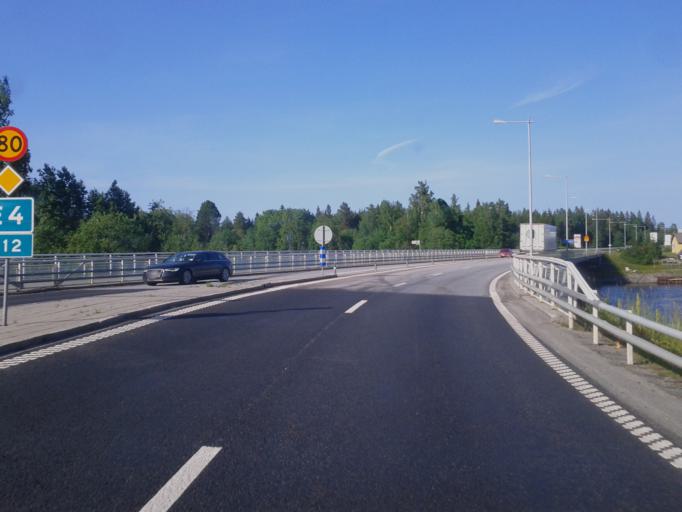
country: SE
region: Vaesterbotten
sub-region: Umea Kommun
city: Umea
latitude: 63.7993
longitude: 20.2849
